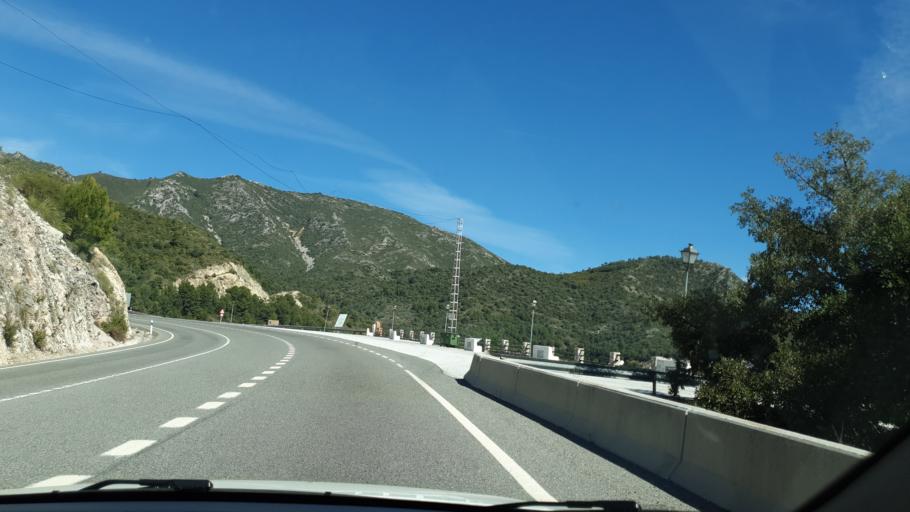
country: ES
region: Andalusia
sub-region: Provincia de Malaga
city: Ojen
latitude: 36.5591
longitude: -4.8609
